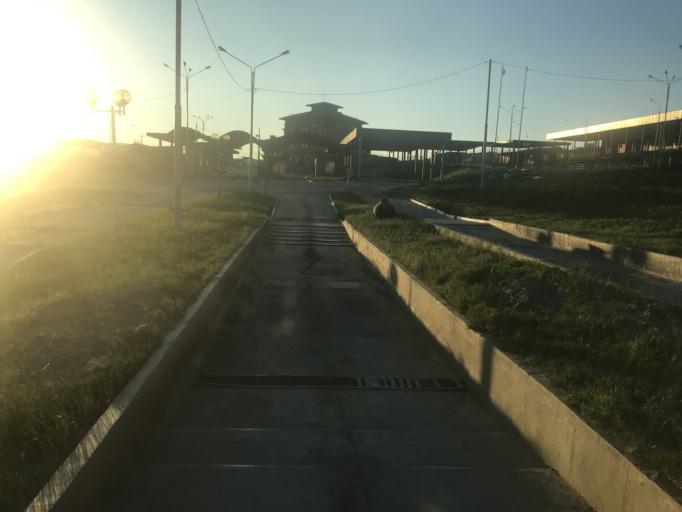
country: MN
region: Selenge
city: Altanbulag
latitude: 50.3245
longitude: 106.4884
